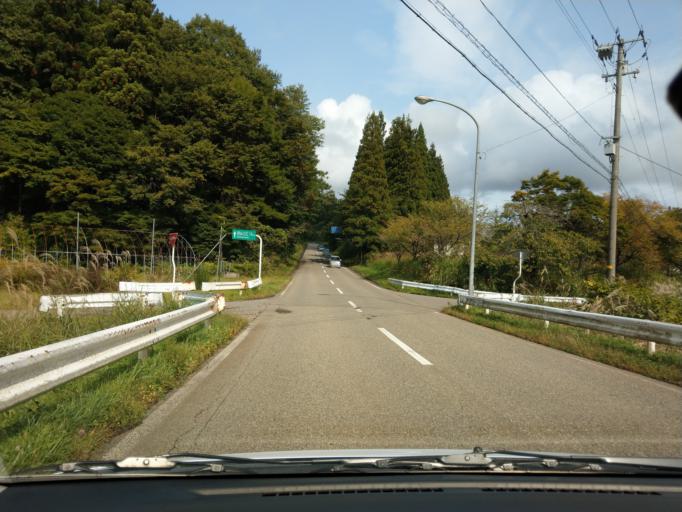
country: JP
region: Akita
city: Omagari
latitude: 39.4660
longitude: 140.3177
